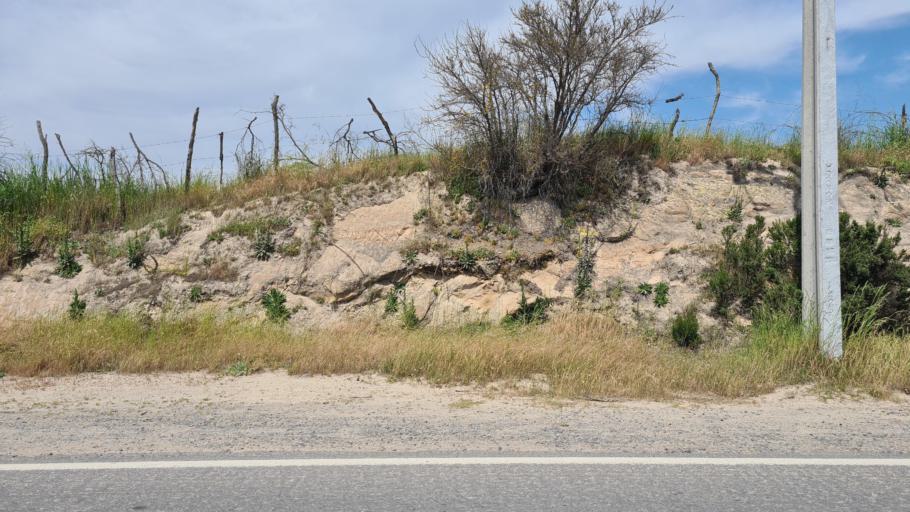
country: CL
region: O'Higgins
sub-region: Provincia de Cachapoal
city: San Vicente
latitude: -34.1617
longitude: -71.4290
